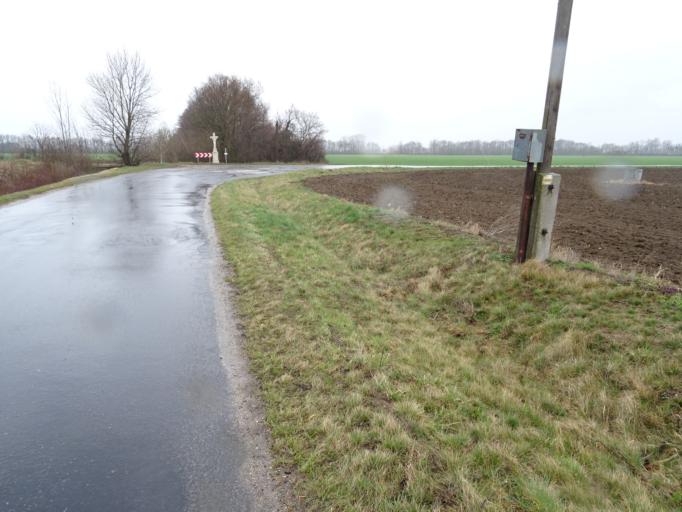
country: AT
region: Burgenland
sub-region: Politischer Bezirk Oberpullendorf
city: Nikitsch
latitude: 47.4878
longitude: 16.7189
